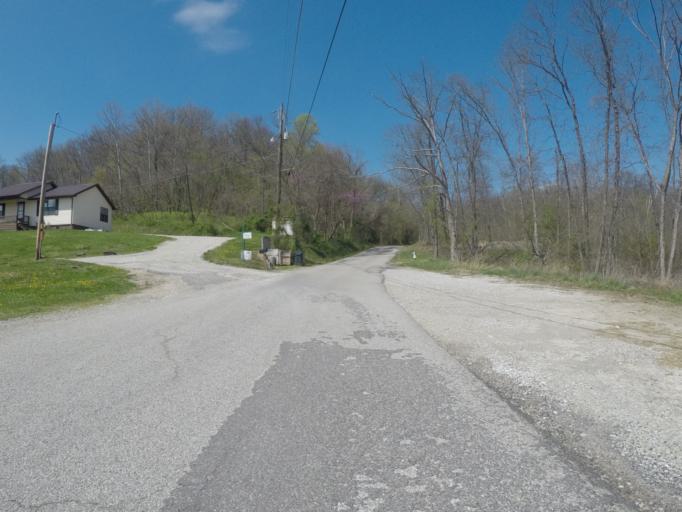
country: US
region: Ohio
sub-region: Lawrence County
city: Burlington
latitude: 38.3795
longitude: -82.5326
